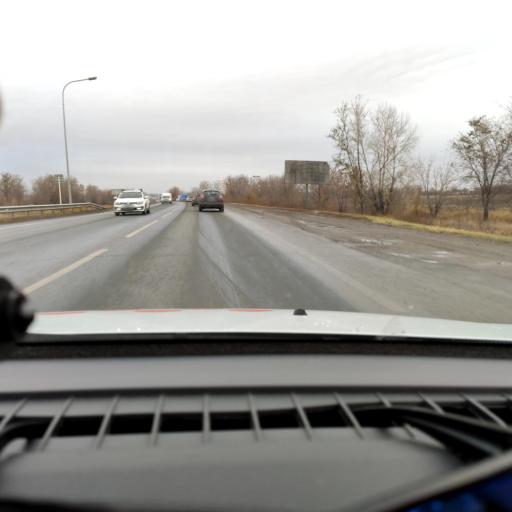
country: RU
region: Samara
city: Samara
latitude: 53.0860
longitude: 50.1428
